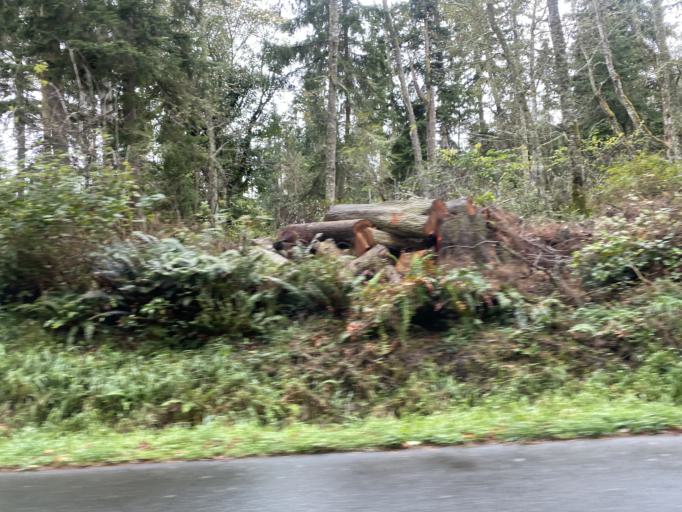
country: US
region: Washington
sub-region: Island County
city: Freeland
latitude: 48.0915
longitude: -122.4902
